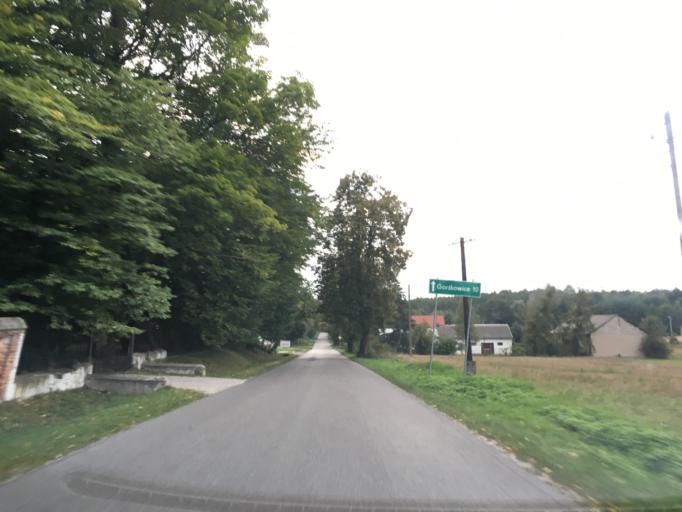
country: PL
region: Lodz Voivodeship
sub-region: Powiat piotrkowski
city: Leki Szlacheckie
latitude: 51.2100
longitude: 19.7241
